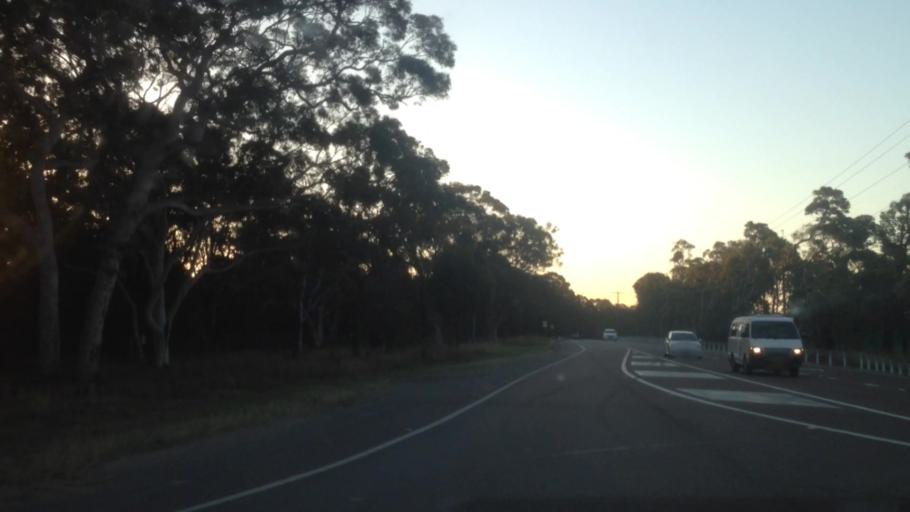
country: AU
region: New South Wales
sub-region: Wyong Shire
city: Kingfisher Shores
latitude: -33.1710
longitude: 151.5364
